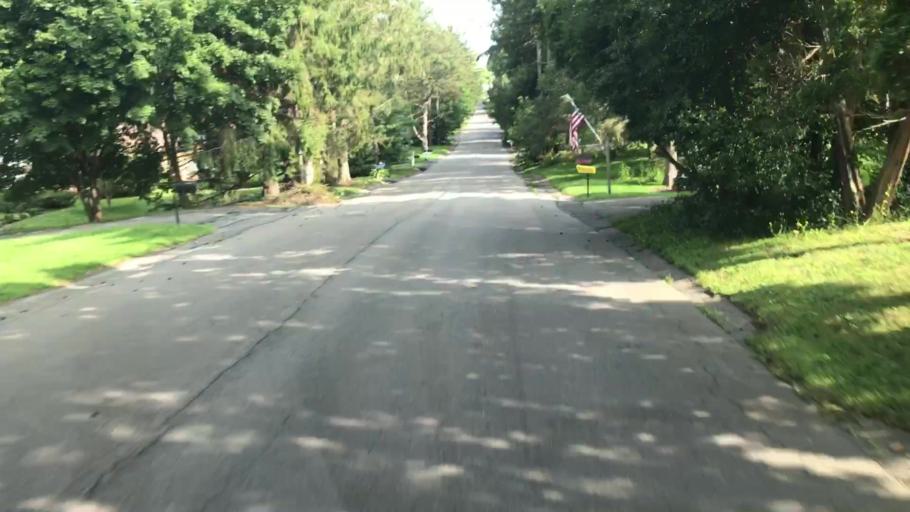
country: US
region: New York
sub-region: Onondaga County
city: Fayetteville
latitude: 43.0343
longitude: -76.0467
